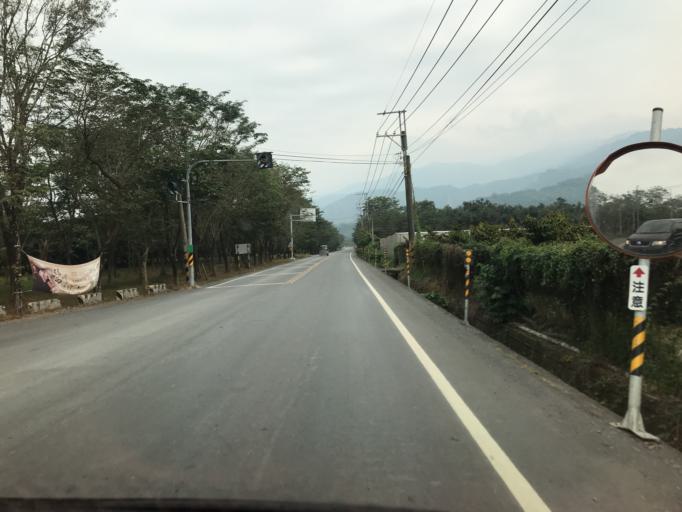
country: TW
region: Taiwan
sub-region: Pingtung
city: Pingtung
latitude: 22.4517
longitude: 120.6096
